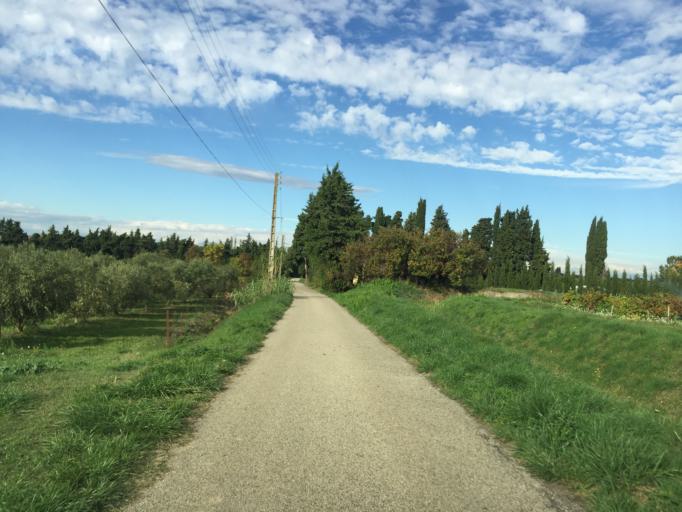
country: FR
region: Provence-Alpes-Cote d'Azur
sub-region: Departement du Vaucluse
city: Orange
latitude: 44.0964
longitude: 4.8121
